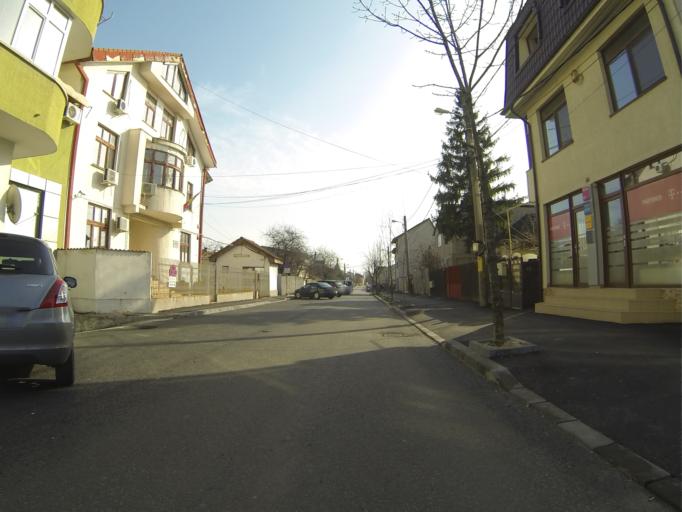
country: RO
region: Dolj
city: Craiova
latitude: 44.3125
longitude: 23.8117
